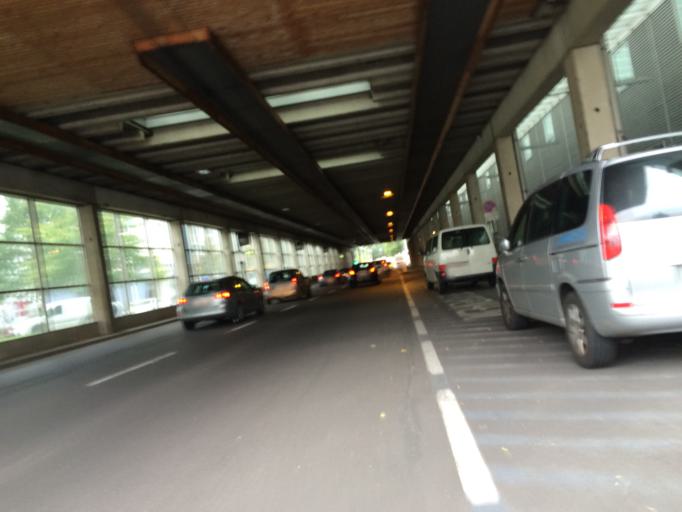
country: AT
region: Upper Austria
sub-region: Linz Stadt
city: Linz
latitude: 48.2906
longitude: 14.3020
